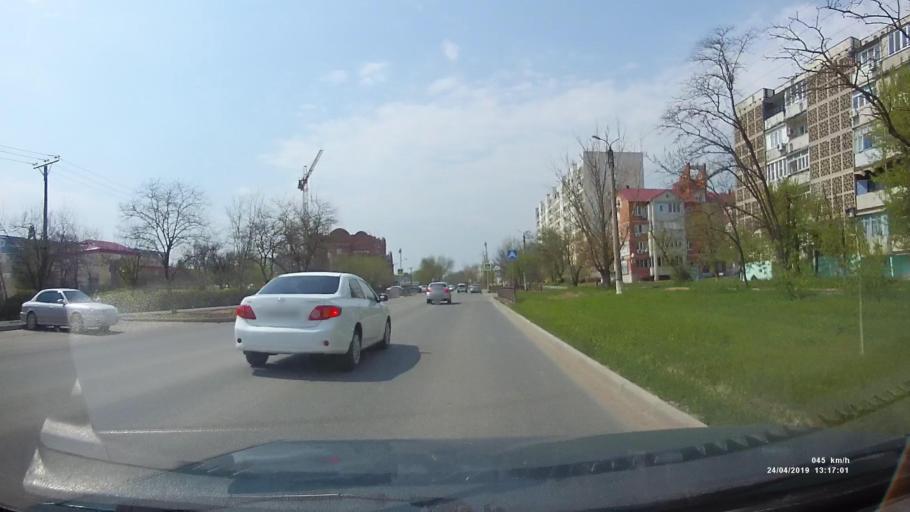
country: RU
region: Kalmykiya
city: Elista
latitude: 46.3050
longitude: 44.3018
